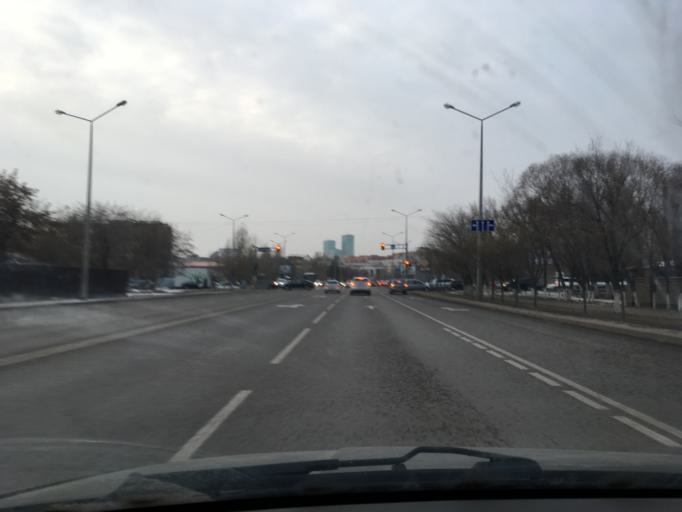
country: KZ
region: Astana Qalasy
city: Astana
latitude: 51.1579
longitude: 71.4455
